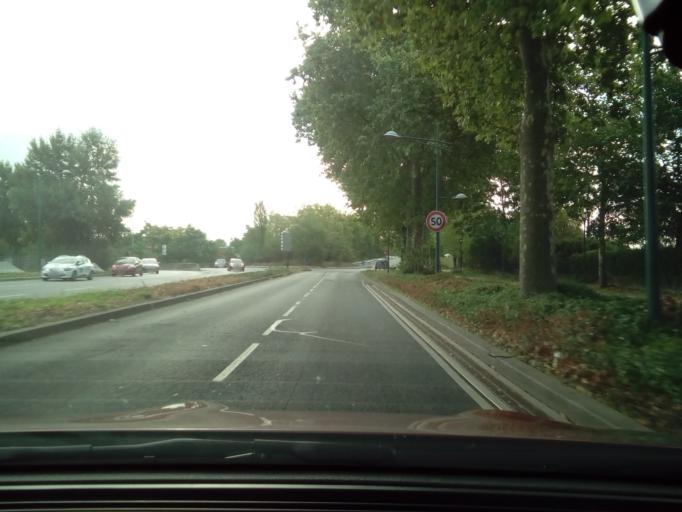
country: FR
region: Rhone-Alpes
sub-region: Departement du Rhone
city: Villeurbanne
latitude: 45.7874
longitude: 4.8848
